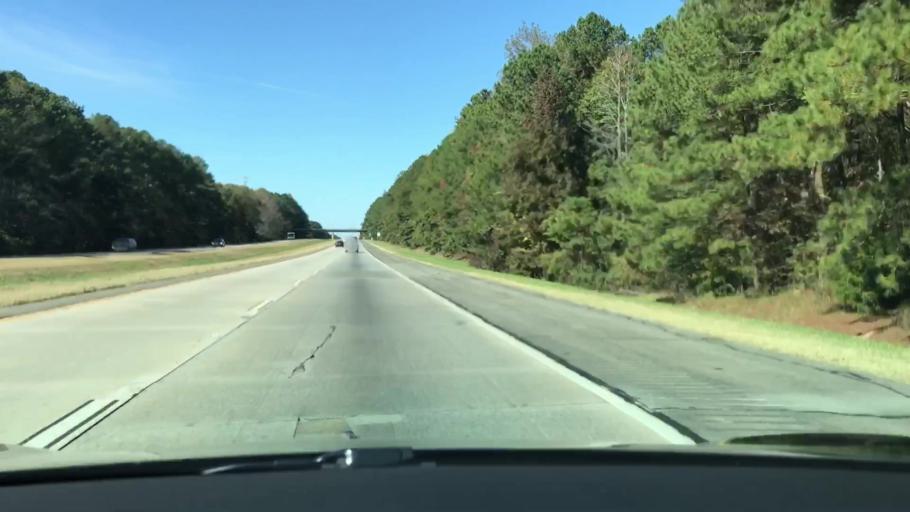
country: US
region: Georgia
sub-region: Greene County
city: Union Point
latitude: 33.5389
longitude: -83.0028
